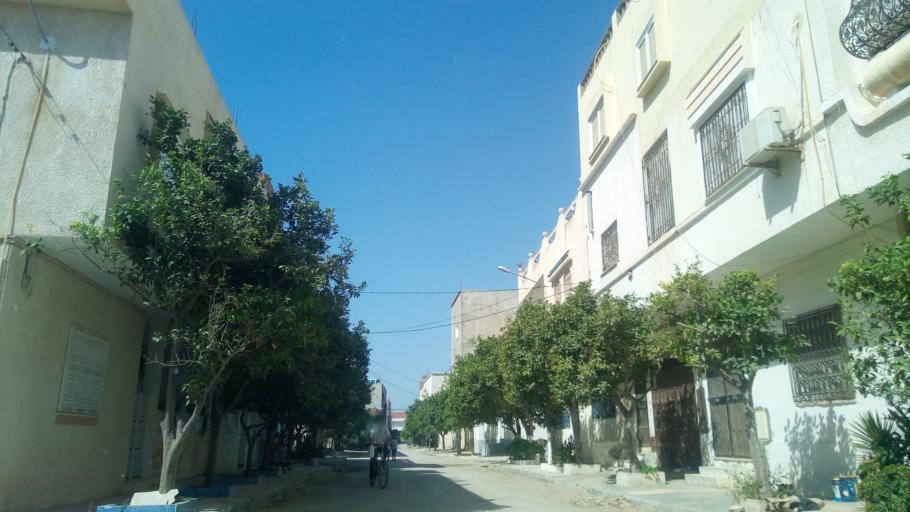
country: TN
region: Nabul
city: Dar Chabanne
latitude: 36.4674
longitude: 10.7427
